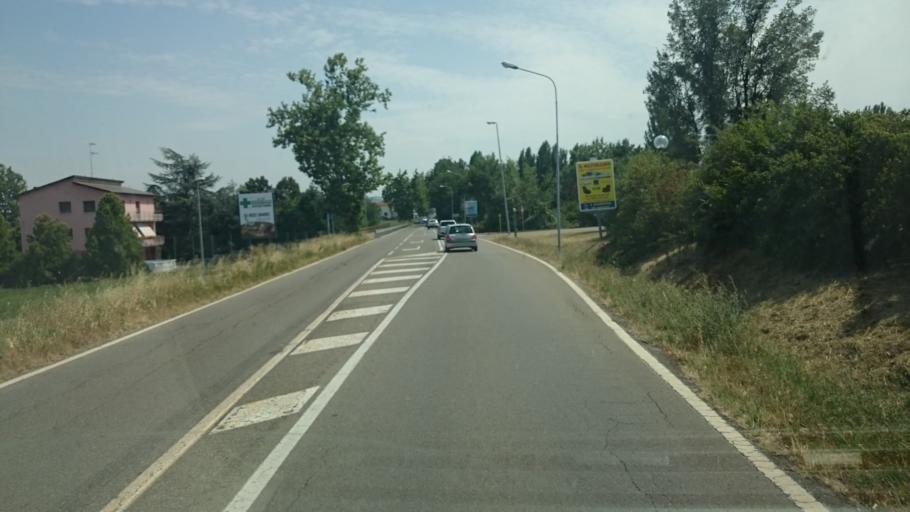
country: IT
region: Emilia-Romagna
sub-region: Provincia di Reggio Emilia
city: Pratissolo
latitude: 44.6257
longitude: 10.6673
